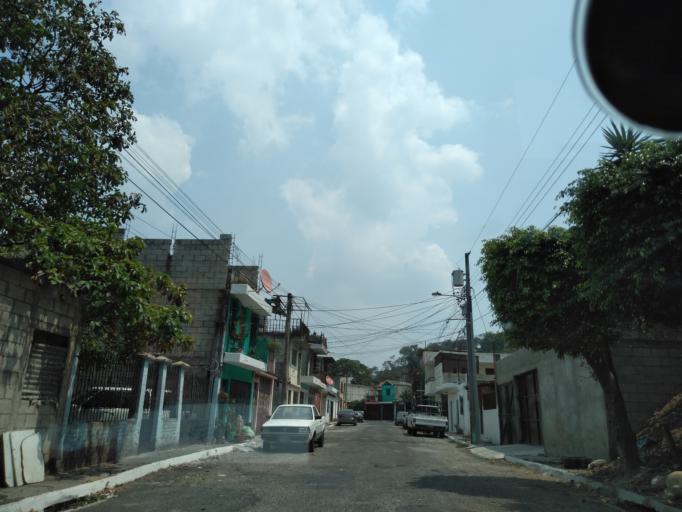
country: GT
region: Guatemala
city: Petapa
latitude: 14.5242
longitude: -90.5403
